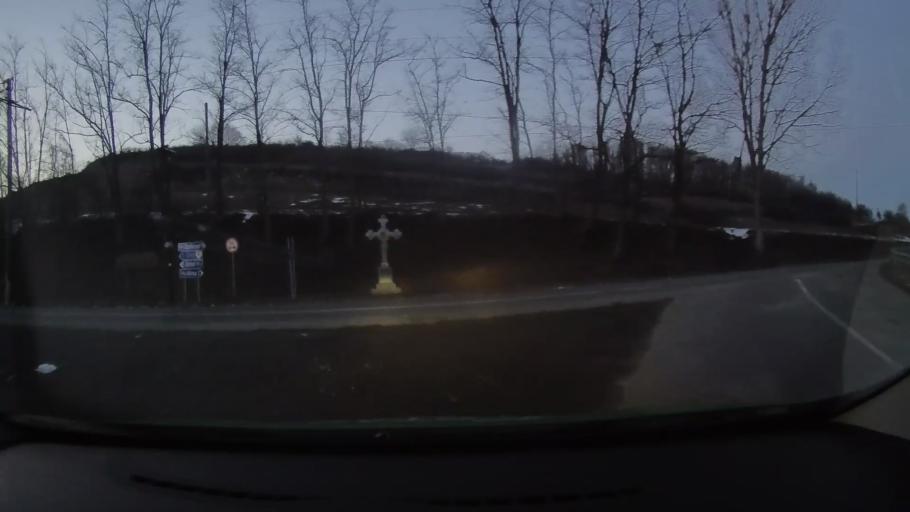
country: RO
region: Sibiu
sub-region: Comuna Alma
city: Alma
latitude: 46.2028
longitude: 24.4673
